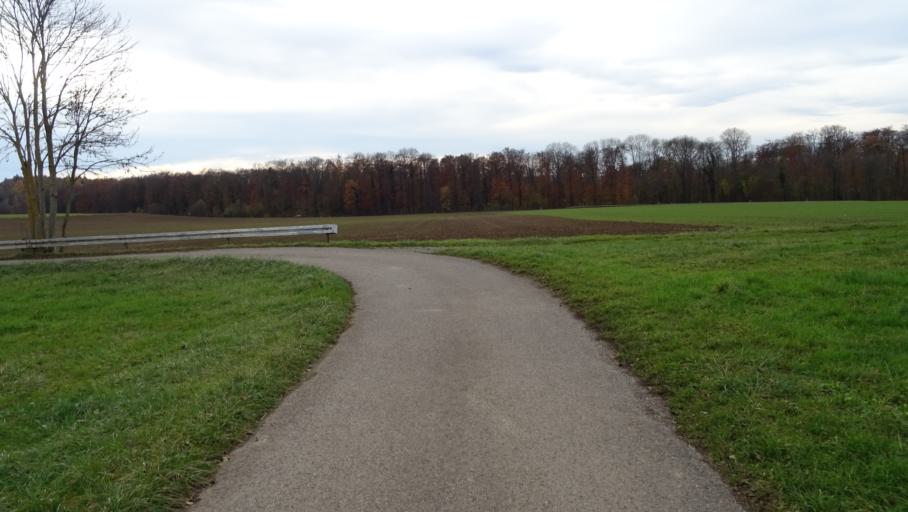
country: DE
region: Baden-Wuerttemberg
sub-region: Karlsruhe Region
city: Mosbach
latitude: 49.3424
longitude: 9.1504
